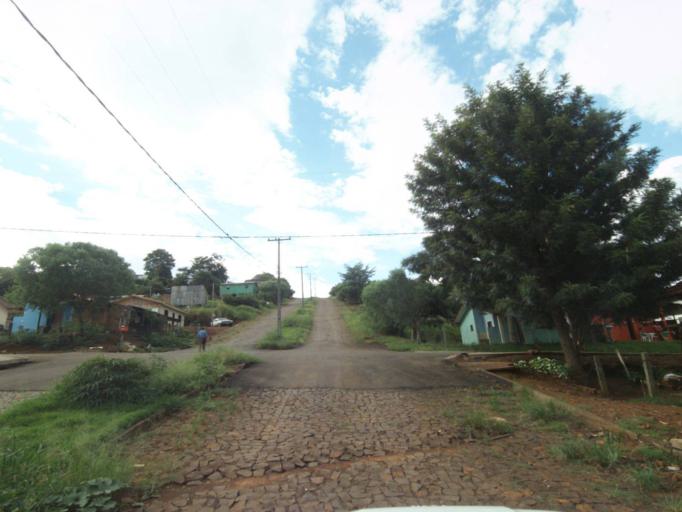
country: BR
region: Parana
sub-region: Laranjeiras Do Sul
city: Laranjeiras do Sul
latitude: -25.4944
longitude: -52.5236
